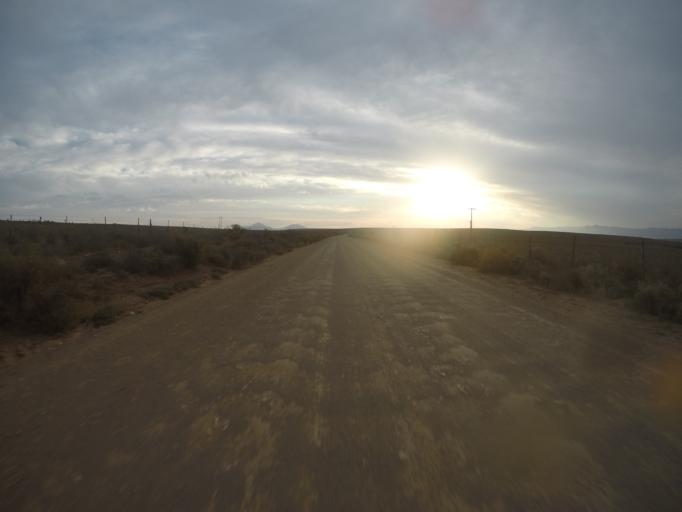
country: ZA
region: Eastern Cape
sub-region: Cacadu District Municipality
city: Willowmore
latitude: -33.5762
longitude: 23.1714
